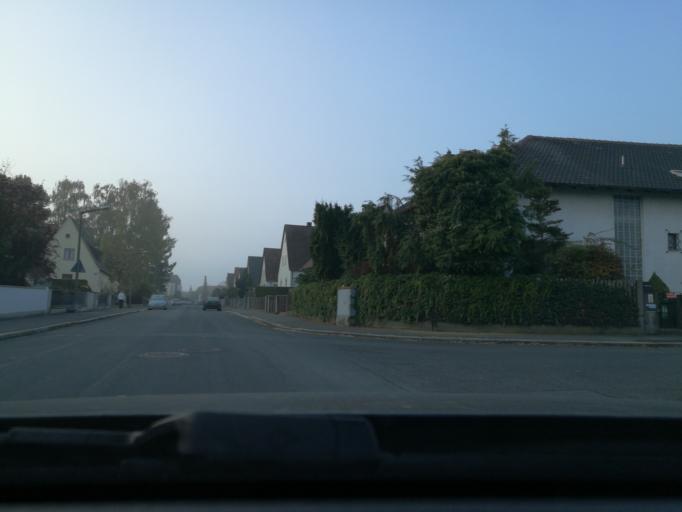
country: DE
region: Bavaria
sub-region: Regierungsbezirk Mittelfranken
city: Furth
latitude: 49.4885
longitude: 10.9648
